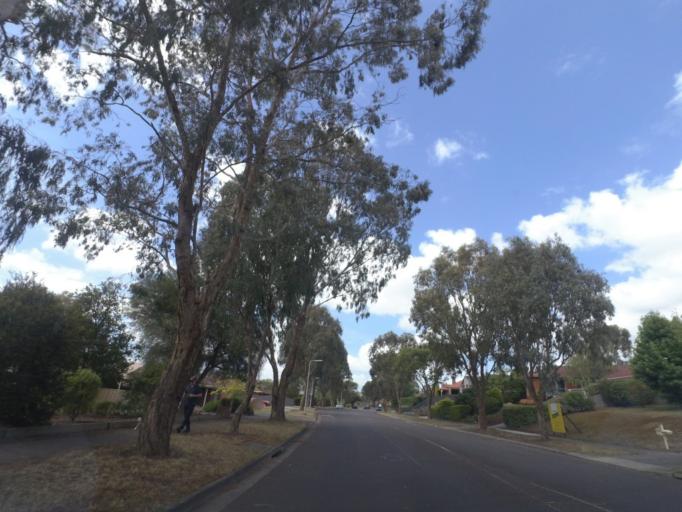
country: AU
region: Victoria
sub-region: Yarra Ranges
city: Lilydale
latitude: -37.7735
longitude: 145.3492
